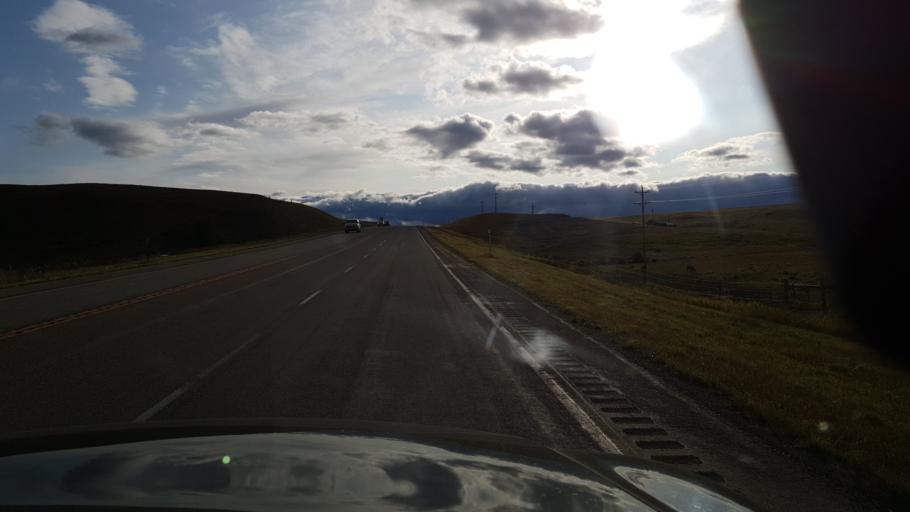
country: US
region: Montana
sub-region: Glacier County
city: South Browning
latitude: 48.5209
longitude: -113.0744
